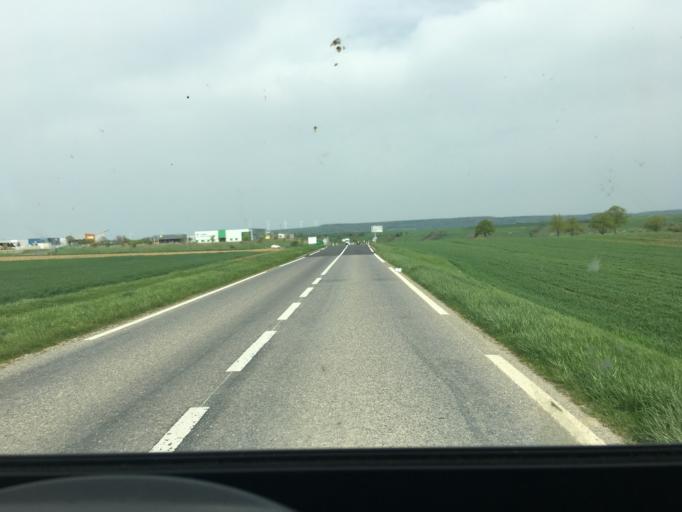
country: FR
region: Lorraine
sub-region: Departement de la Moselle
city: Vic-sur-Seille
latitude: 48.8082
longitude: 6.5450
